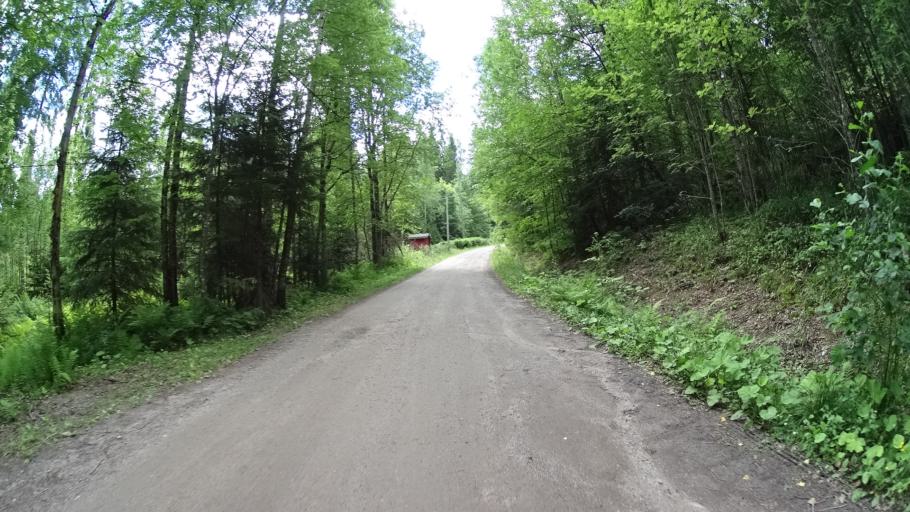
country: FI
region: Uusimaa
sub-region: Helsinki
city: Espoo
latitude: 60.2982
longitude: 24.6210
